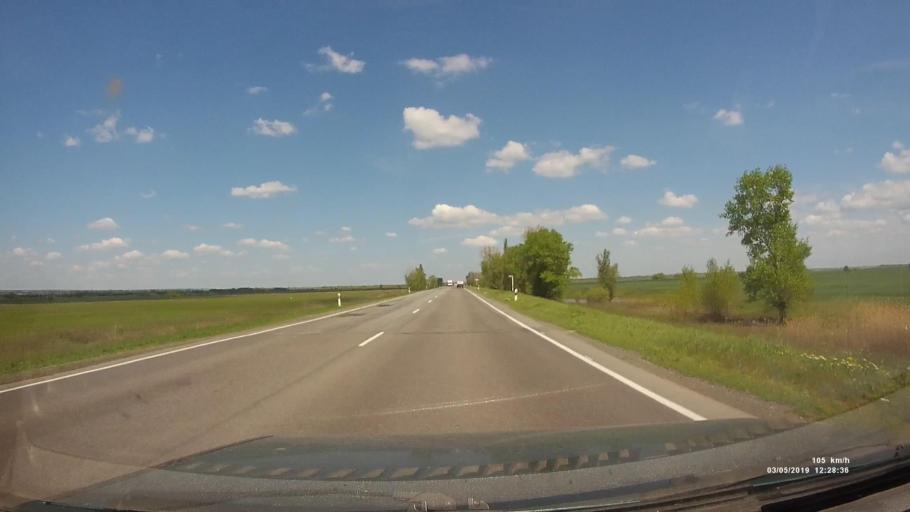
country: RU
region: Rostov
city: Semikarakorsk
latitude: 47.4759
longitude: 40.7301
